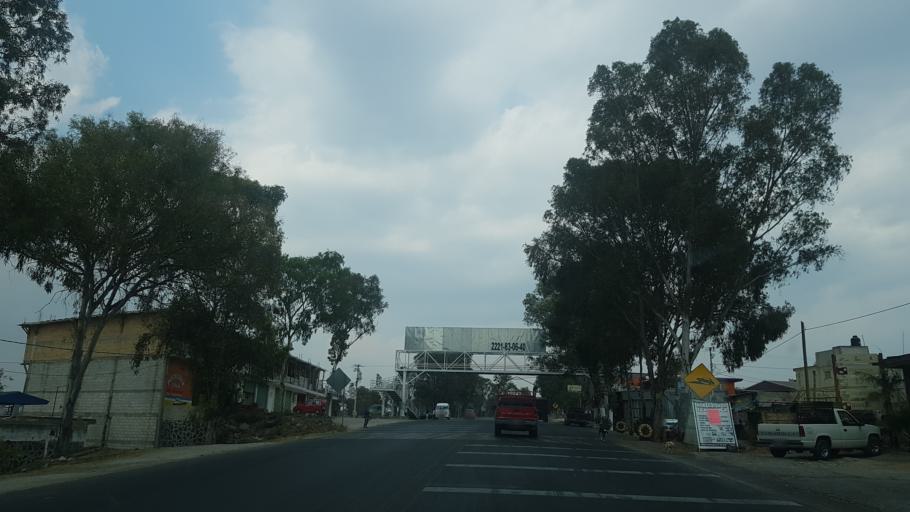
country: MX
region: Puebla
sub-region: Santa Isabel Cholula
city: San Pablo Ahuatempa
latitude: 18.9841
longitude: -98.3654
